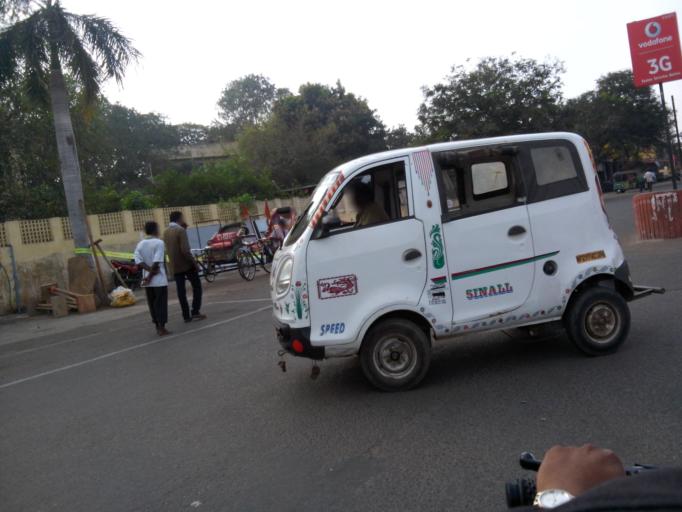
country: IN
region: Andhra Pradesh
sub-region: Krishna
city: Vijayawada
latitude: 16.5148
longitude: 80.6178
